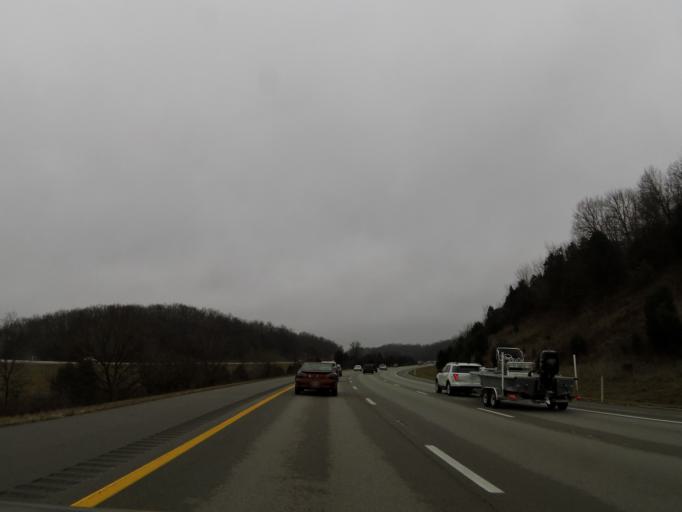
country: US
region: Kentucky
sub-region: Scott County
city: Georgetown
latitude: 38.3336
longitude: -84.5646
